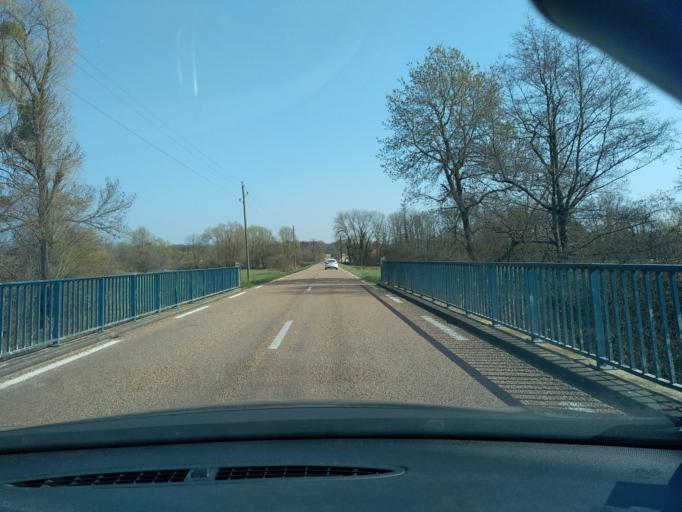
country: FR
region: Franche-Comte
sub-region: Departement du Jura
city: Mont-sous-Vaudrey
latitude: 46.9503
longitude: 5.5106
